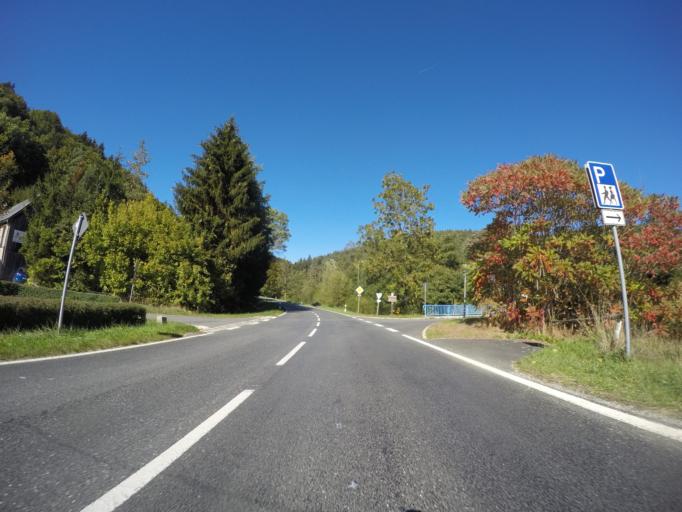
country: DE
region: Bavaria
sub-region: Upper Franconia
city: Gossweinstein
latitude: 49.7817
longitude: 11.3339
